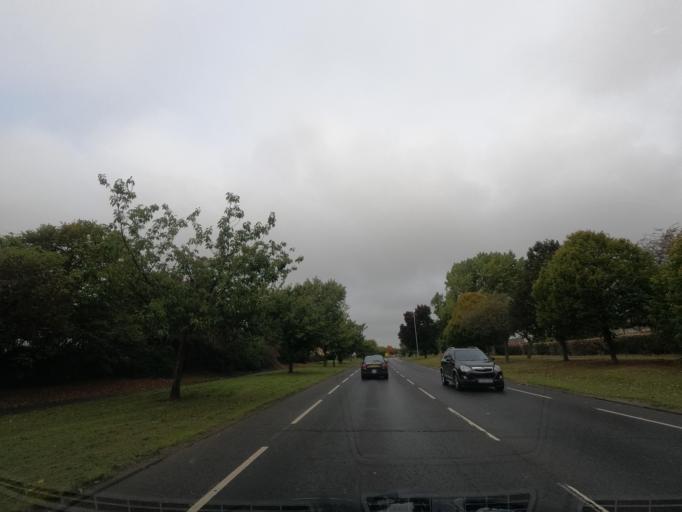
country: GB
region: England
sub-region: Middlesbrough
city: Nunthorpe
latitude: 54.5572
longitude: -1.1879
